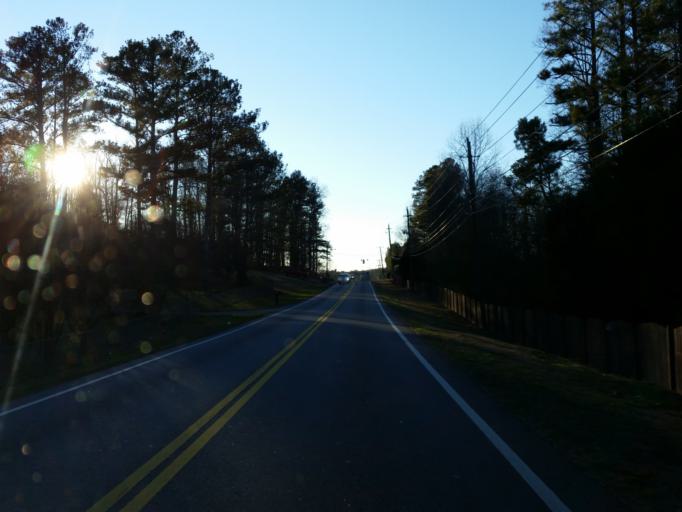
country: US
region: Georgia
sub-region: Cherokee County
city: Woodstock
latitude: 34.1312
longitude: -84.4892
